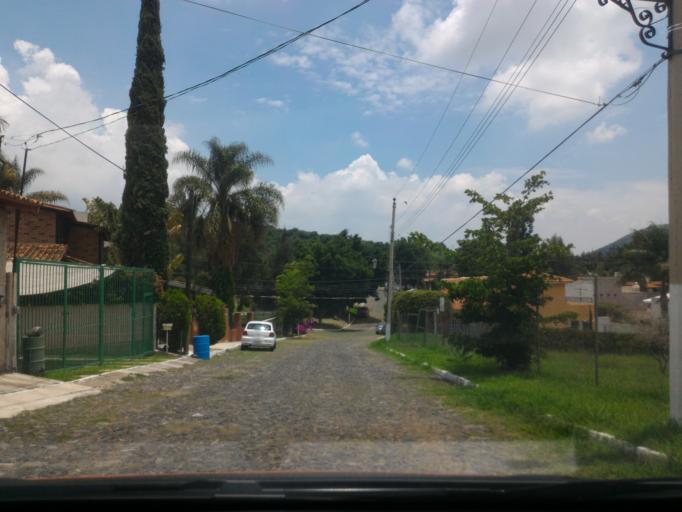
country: MX
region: Jalisco
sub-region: Tlajomulco de Zuniga
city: Santa Cruz de las Flores
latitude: 20.5001
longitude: -103.4980
